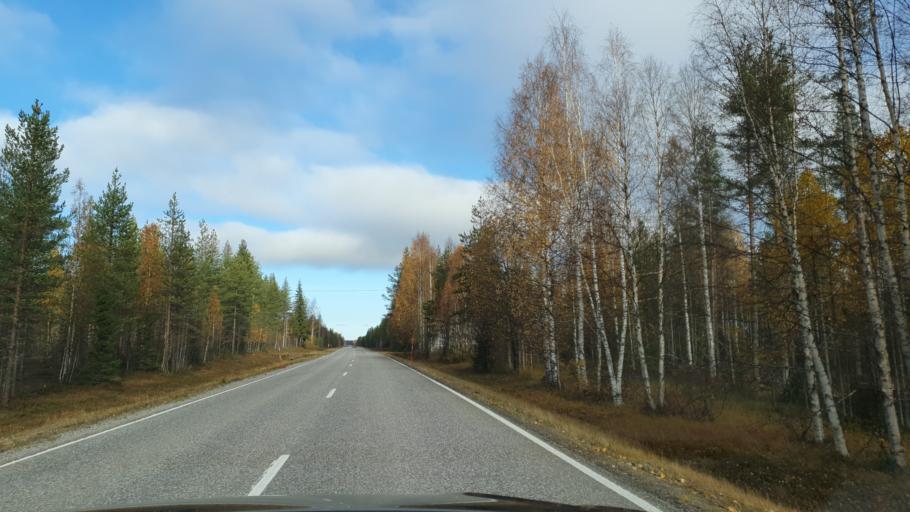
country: FI
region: Lapland
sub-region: Tunturi-Lappi
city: Kittilae
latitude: 67.1930
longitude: 24.9364
